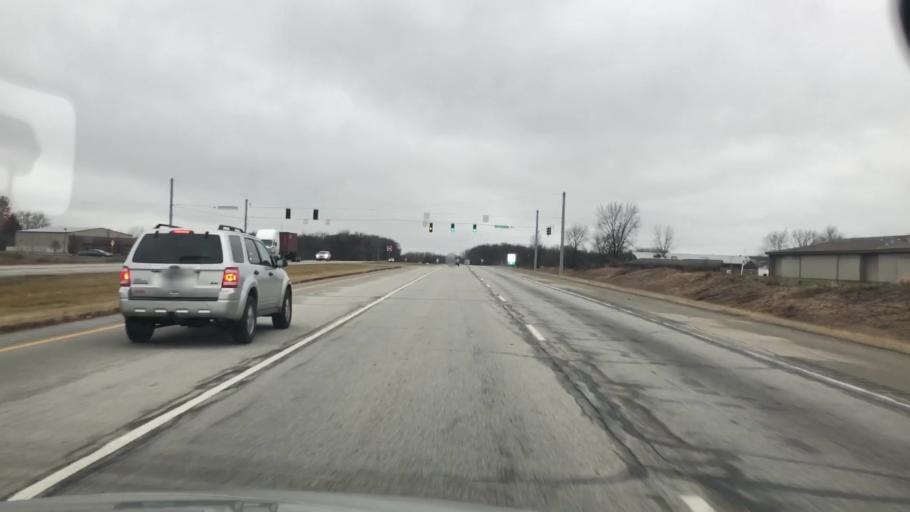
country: US
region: Indiana
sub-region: Kosciusko County
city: Winona Lake
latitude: 41.2524
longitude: -85.8279
